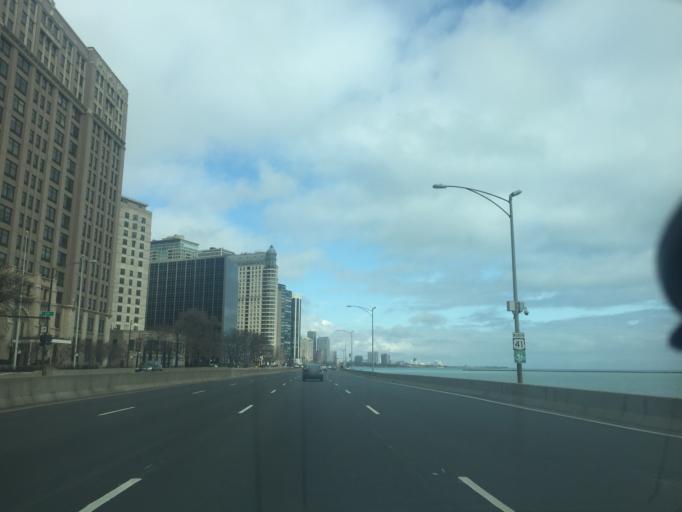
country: US
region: Illinois
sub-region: Cook County
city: Chicago
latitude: 41.8940
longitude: -87.6148
